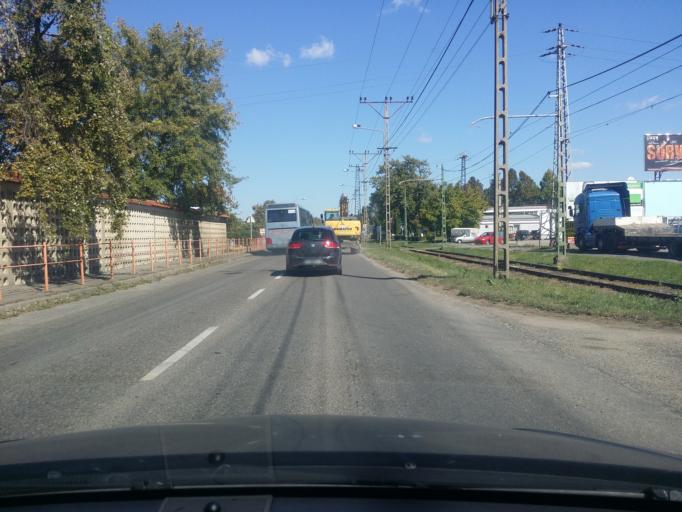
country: HU
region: Csongrad
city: Szeged
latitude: 46.2593
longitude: 20.1070
